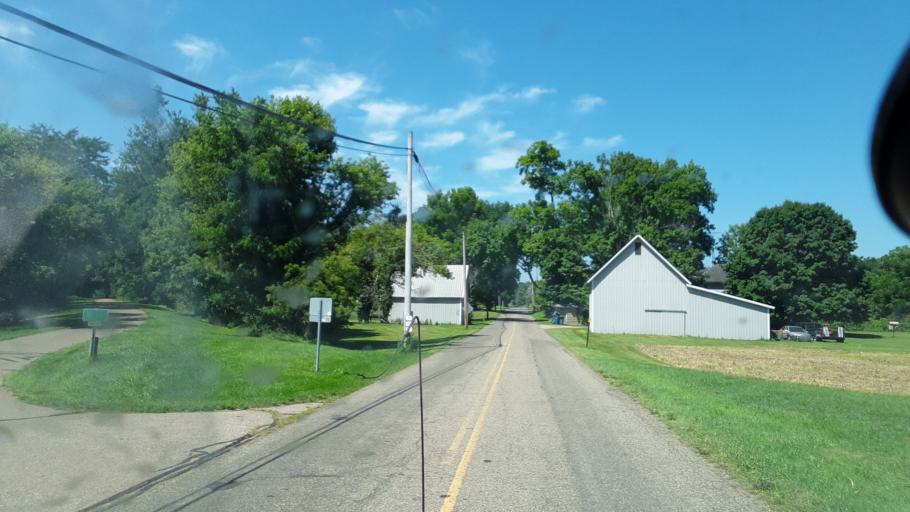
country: US
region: Ohio
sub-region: Knox County
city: Gambier
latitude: 40.3758
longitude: -82.3774
